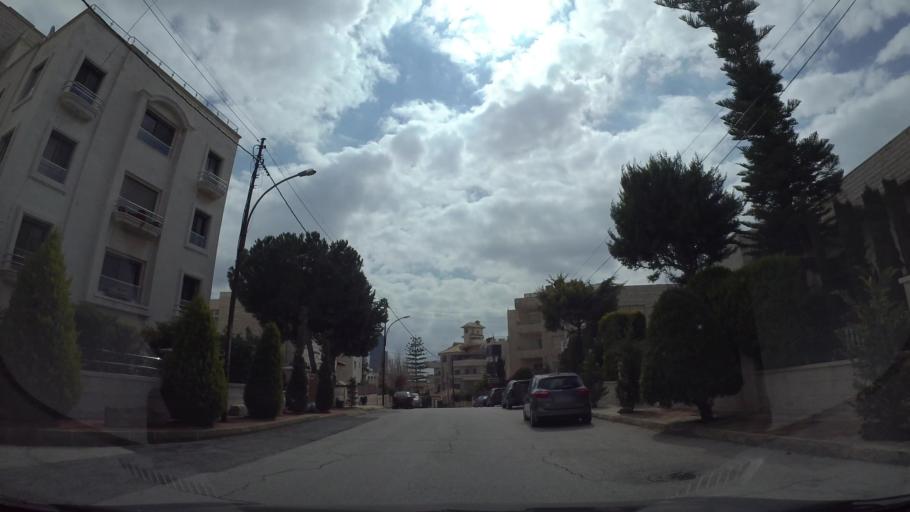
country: JO
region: Amman
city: Amman
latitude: 31.9749
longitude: 35.9026
